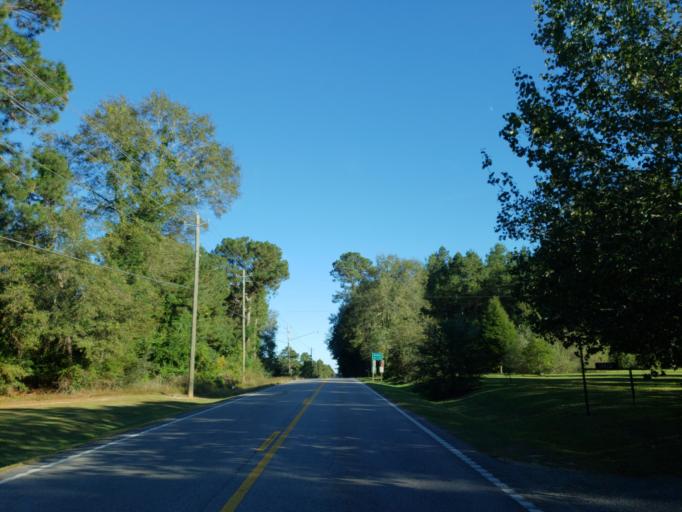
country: US
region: Mississippi
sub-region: Perry County
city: Richton
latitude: 31.3552
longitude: -88.9561
